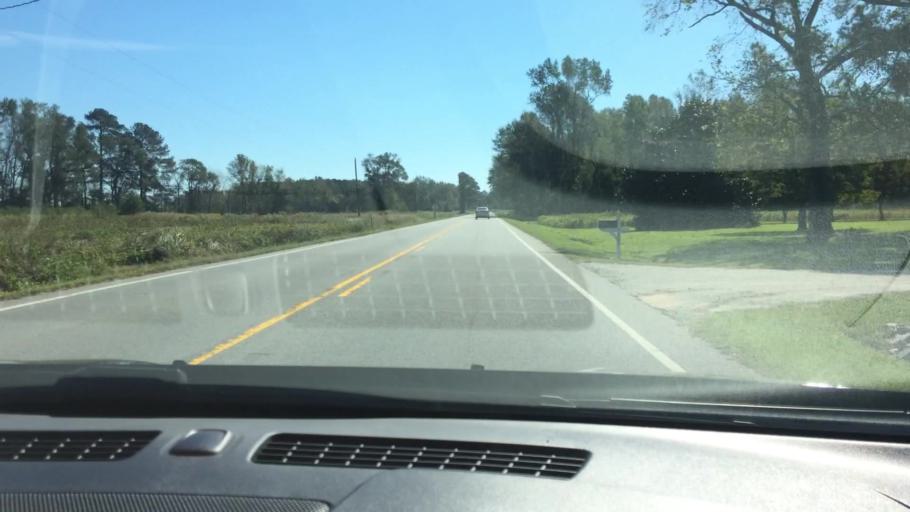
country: US
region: North Carolina
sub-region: Pitt County
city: Grifton
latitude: 35.3603
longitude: -77.3447
